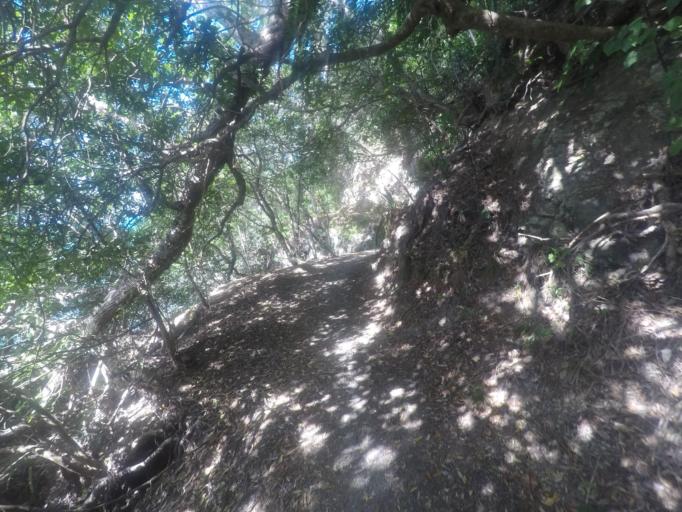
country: NZ
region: Auckland
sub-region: Auckland
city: Warkworth
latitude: -36.2866
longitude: 174.8093
